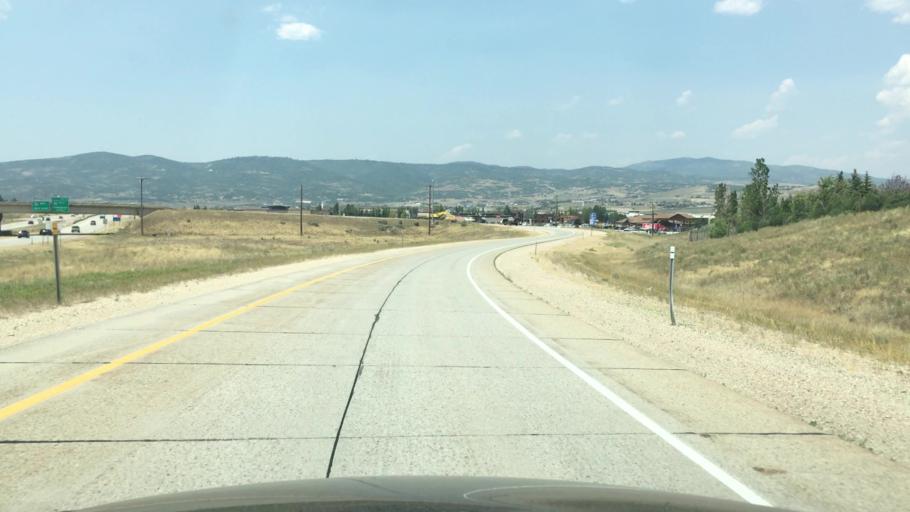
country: US
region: Utah
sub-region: Summit County
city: Snyderville
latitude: 40.7161
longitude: -111.4851
